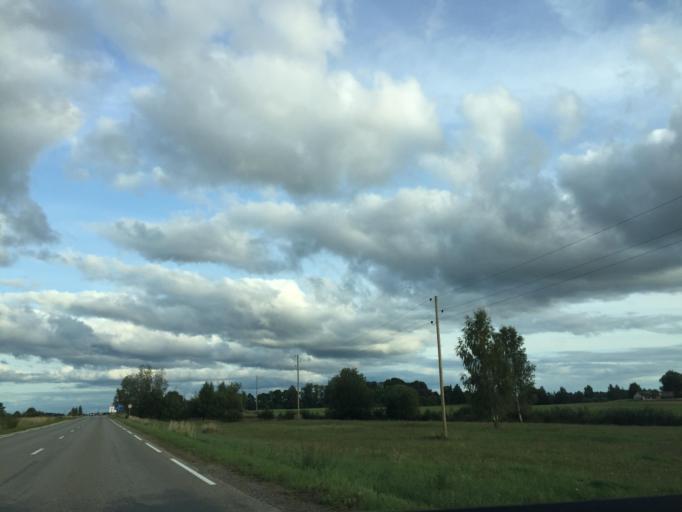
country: LV
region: Nereta
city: Nereta
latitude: 56.2547
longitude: 25.2092
